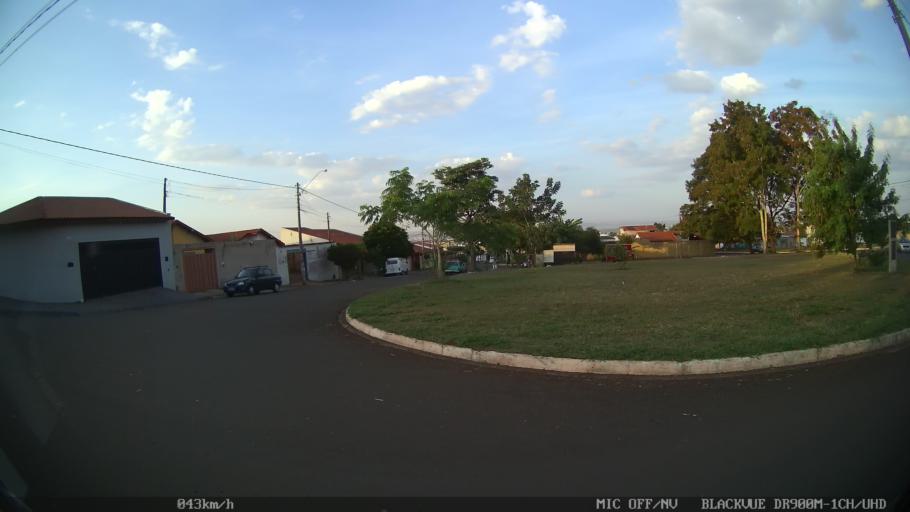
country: BR
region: Sao Paulo
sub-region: Ribeirao Preto
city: Ribeirao Preto
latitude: -21.1460
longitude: -47.8522
